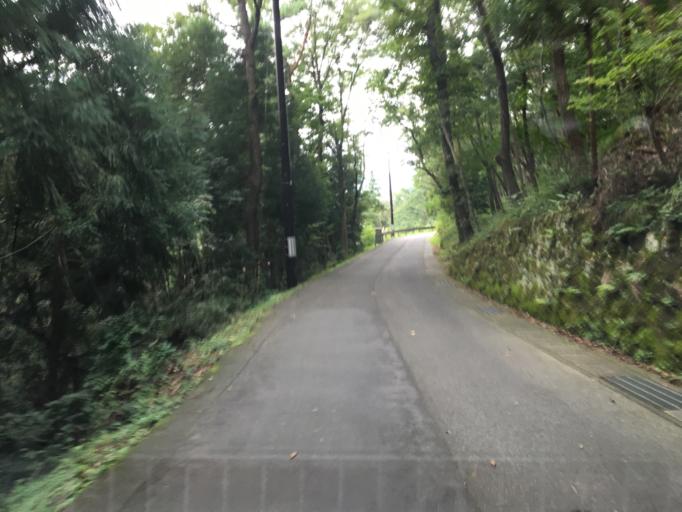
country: JP
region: Fukushima
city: Fukushima-shi
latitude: 37.7750
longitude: 140.4808
